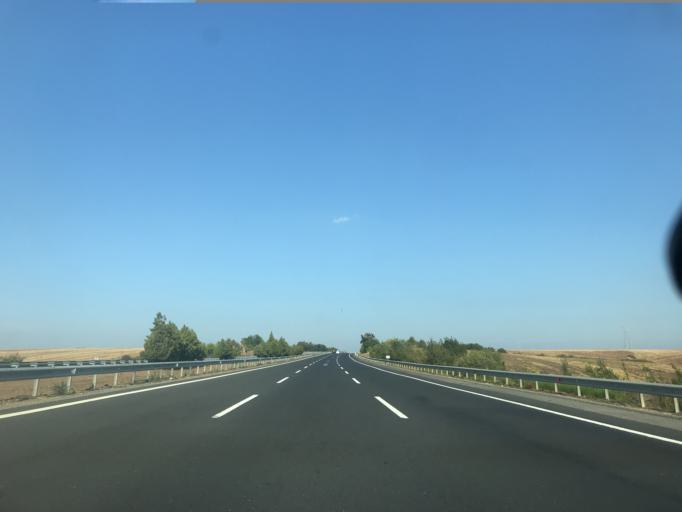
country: TR
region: Kirklareli
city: Luleburgaz
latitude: 41.4748
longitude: 27.3155
